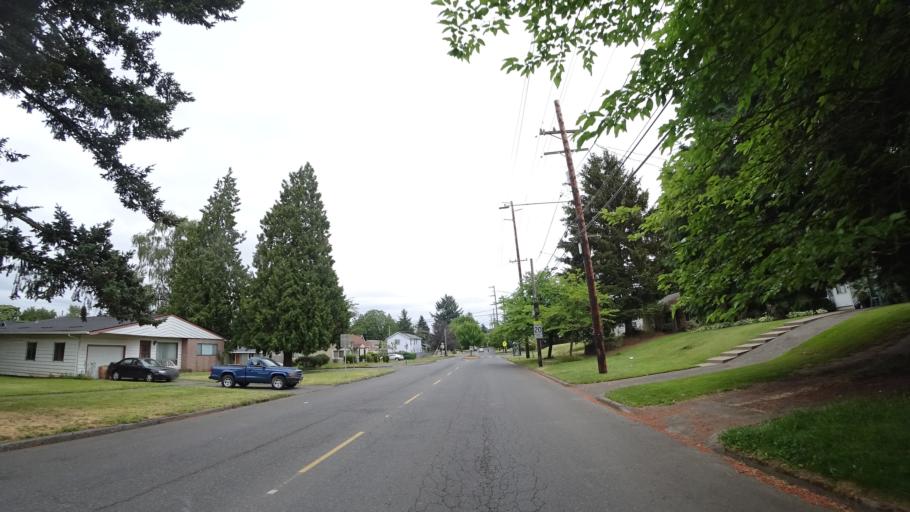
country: US
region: Oregon
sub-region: Multnomah County
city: Portland
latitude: 45.5840
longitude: -122.7010
